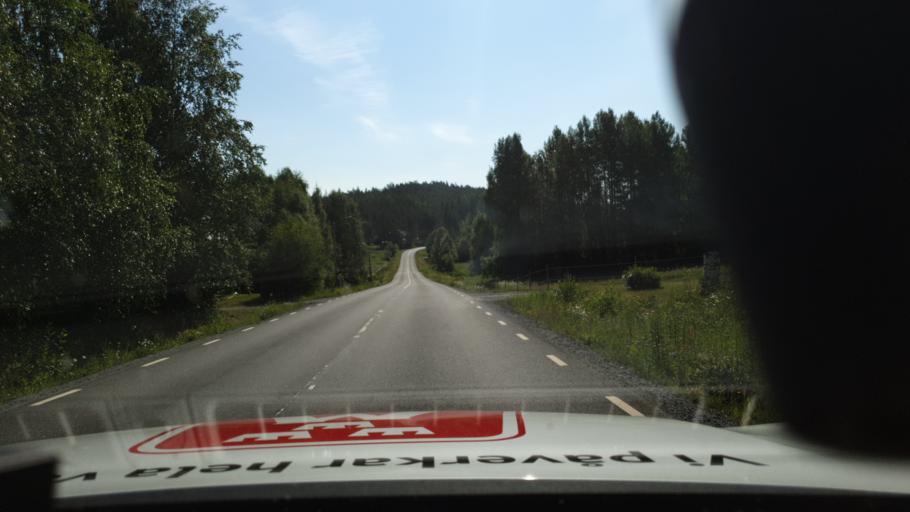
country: SE
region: Norrbotten
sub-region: Bodens Kommun
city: Saevast
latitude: 65.8317
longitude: 21.8749
